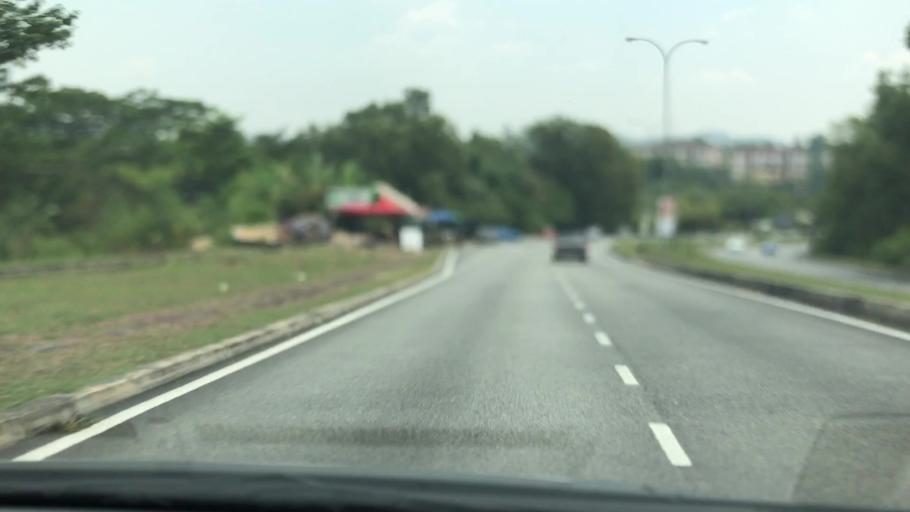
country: MY
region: Putrajaya
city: Putrajaya
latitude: 2.9914
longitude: 101.6634
